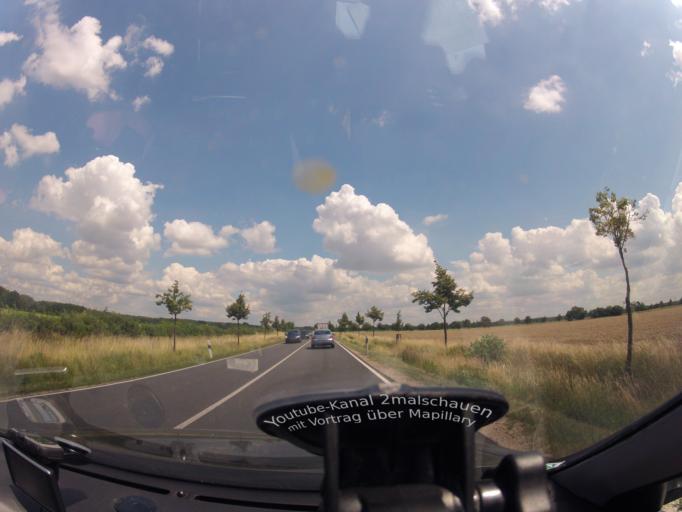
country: DE
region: Saxony
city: Zinna
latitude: 51.5381
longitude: 12.9251
